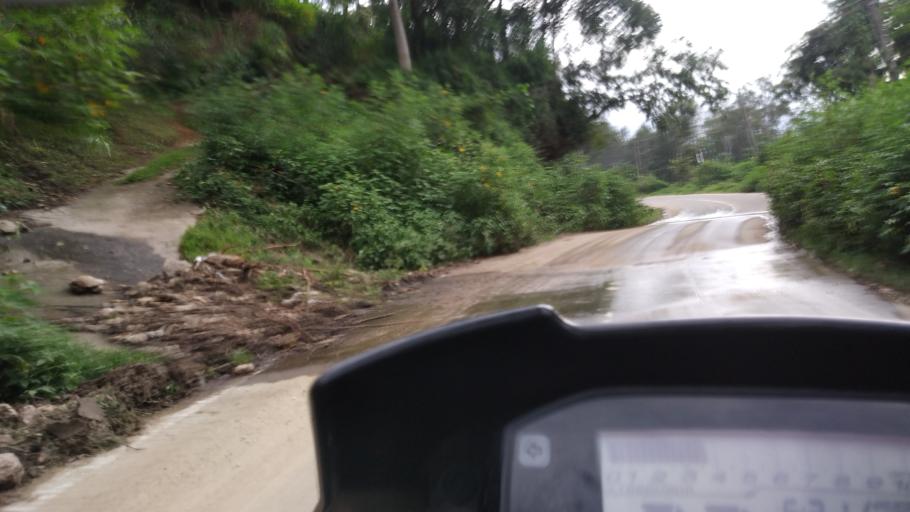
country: IN
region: Tamil Nadu
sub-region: Theni
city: Bodinayakkanur
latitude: 10.0160
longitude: 77.2417
